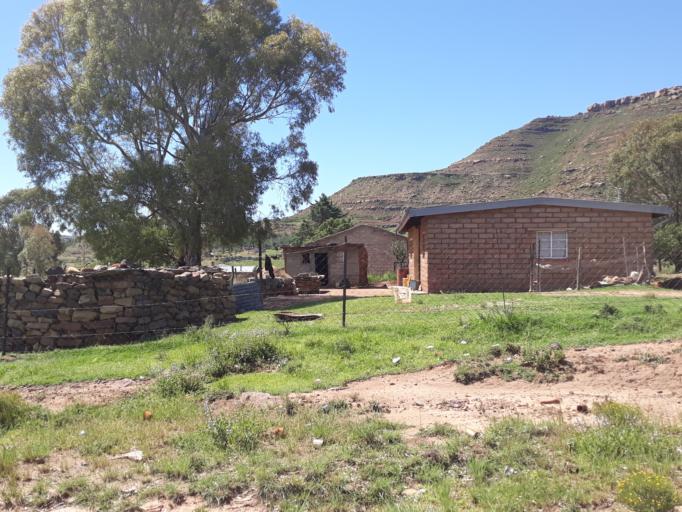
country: LS
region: Quthing
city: Quthing
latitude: -30.3320
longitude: 27.5358
